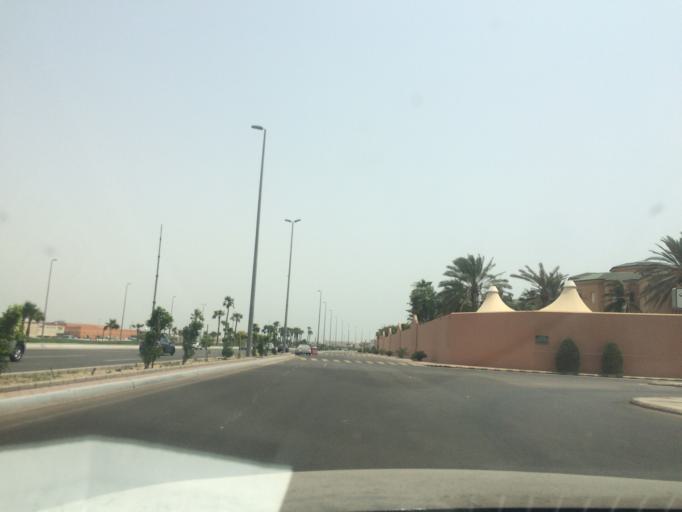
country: SA
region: Makkah
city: Jeddah
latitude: 21.5862
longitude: 39.1254
